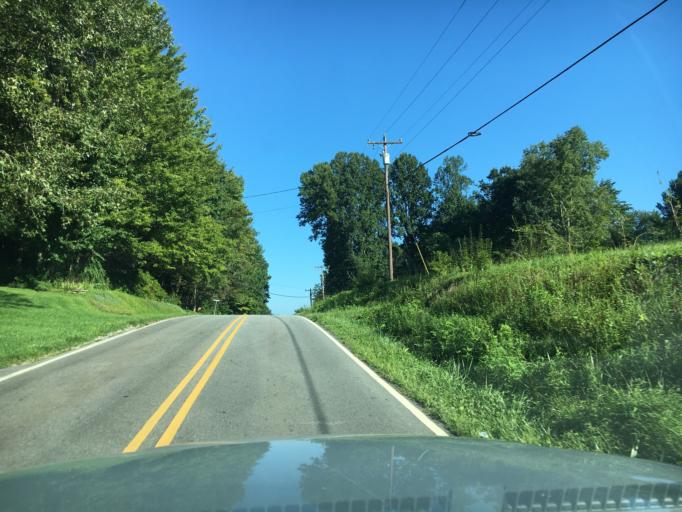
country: US
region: North Carolina
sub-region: McDowell County
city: West Marion
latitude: 35.6568
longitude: -82.0322
